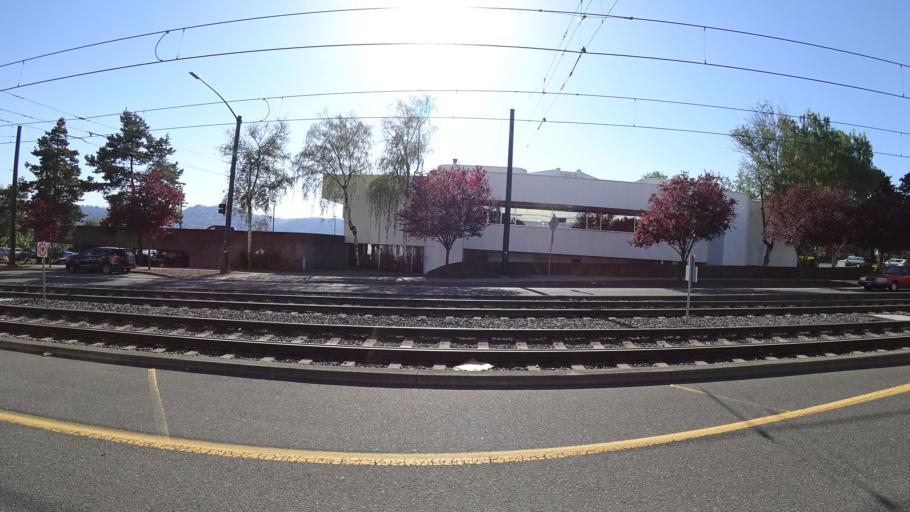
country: US
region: Oregon
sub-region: Multnomah County
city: Portland
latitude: 45.5473
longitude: -122.6809
